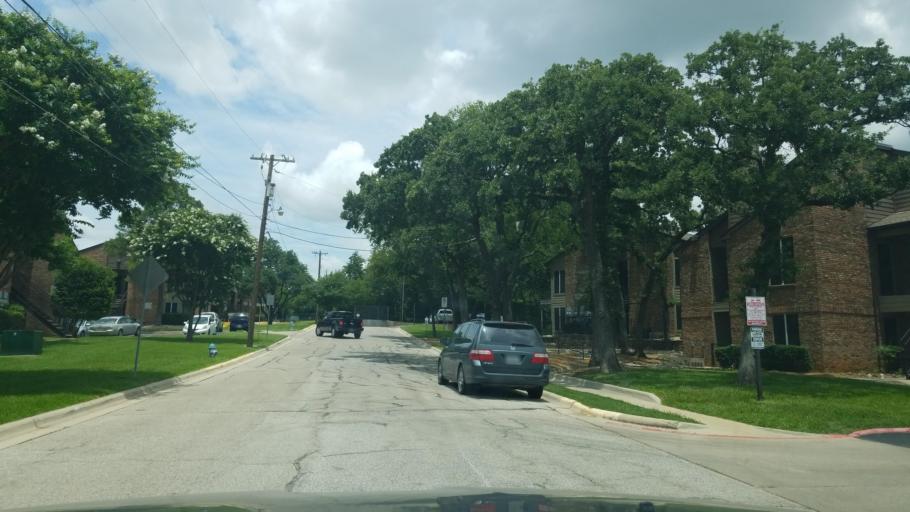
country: US
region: Texas
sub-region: Denton County
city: Denton
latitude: 33.2103
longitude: -97.1402
